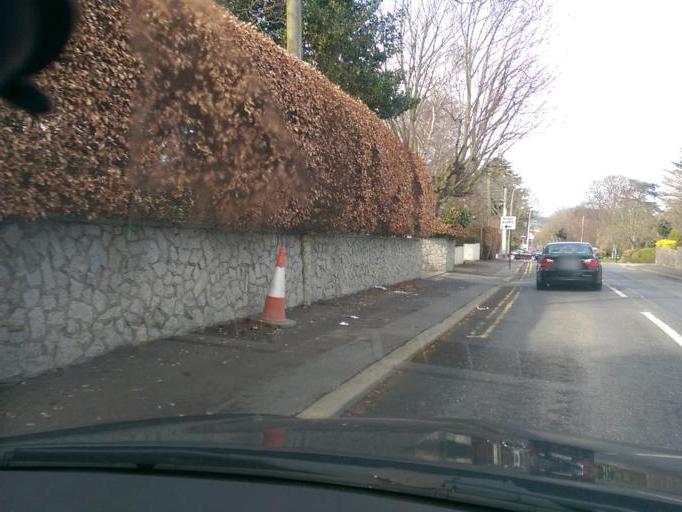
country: IE
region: Leinster
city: Malahide
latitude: 53.4463
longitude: -6.1527
